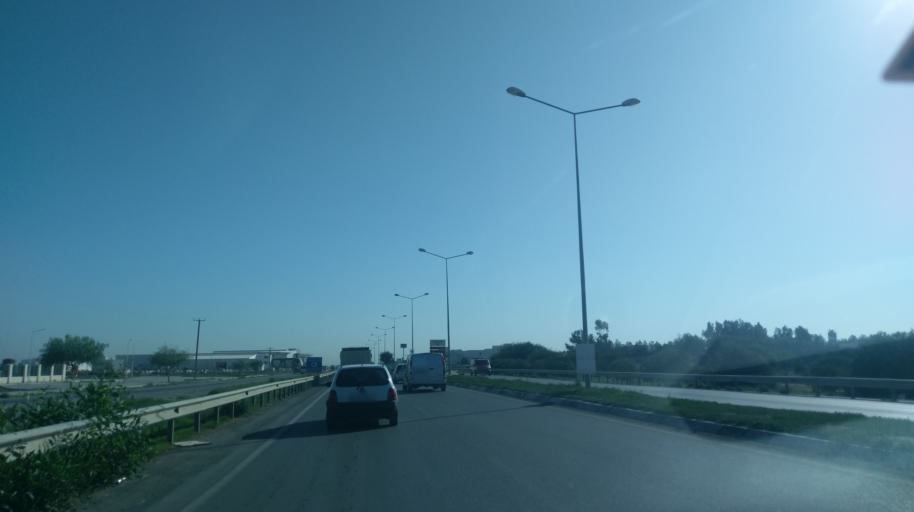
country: CY
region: Lefkosia
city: Nicosia
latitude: 35.2166
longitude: 33.4231
